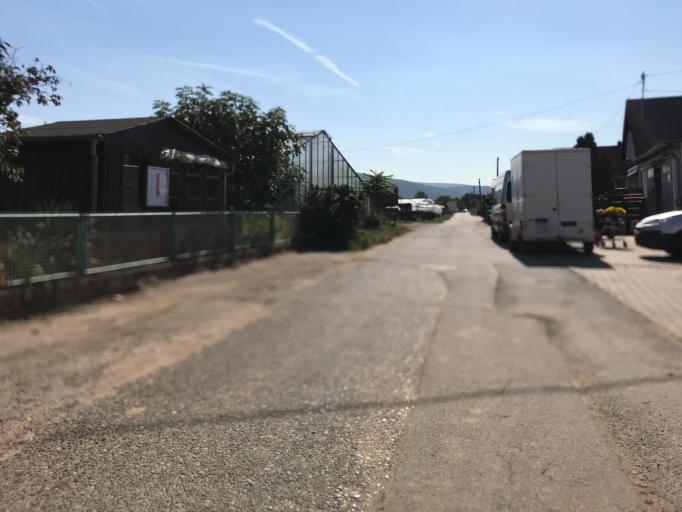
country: DE
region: Baden-Wuerttemberg
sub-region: Karlsruhe Region
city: Dossenheim
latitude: 49.4318
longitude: 8.6728
